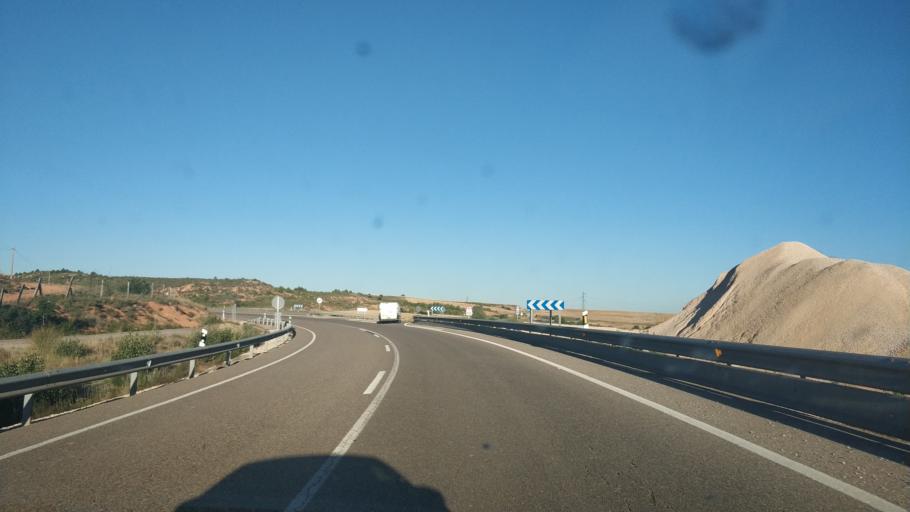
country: ES
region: Castille and Leon
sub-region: Provincia de Soria
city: San Esteban de Gormaz
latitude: 41.5655
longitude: -3.1856
